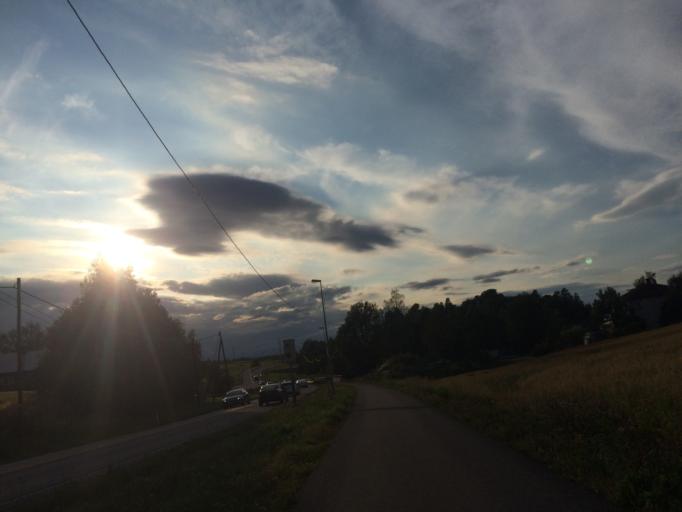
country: NO
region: Akershus
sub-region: Ski
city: Ski
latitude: 59.6719
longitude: 10.8917
